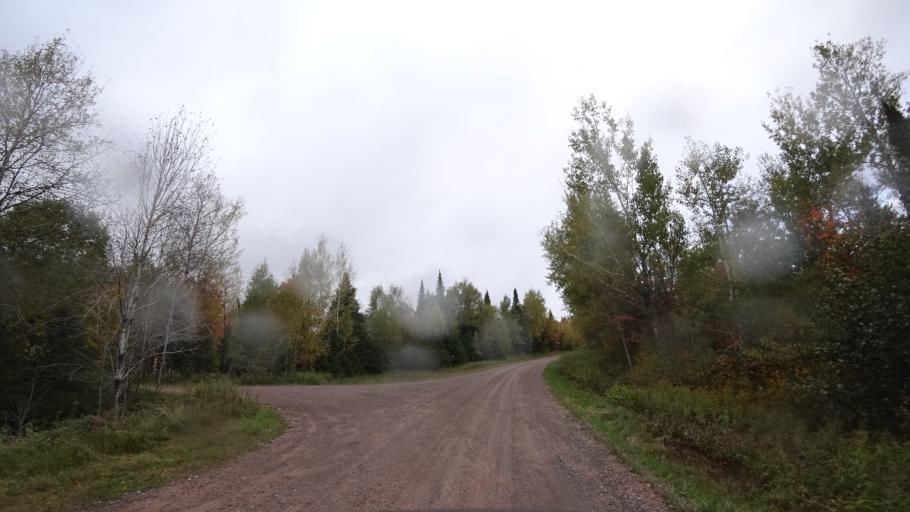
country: US
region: Wisconsin
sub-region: Sawyer County
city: Little Round Lake
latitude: 45.9871
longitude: -91.0003
